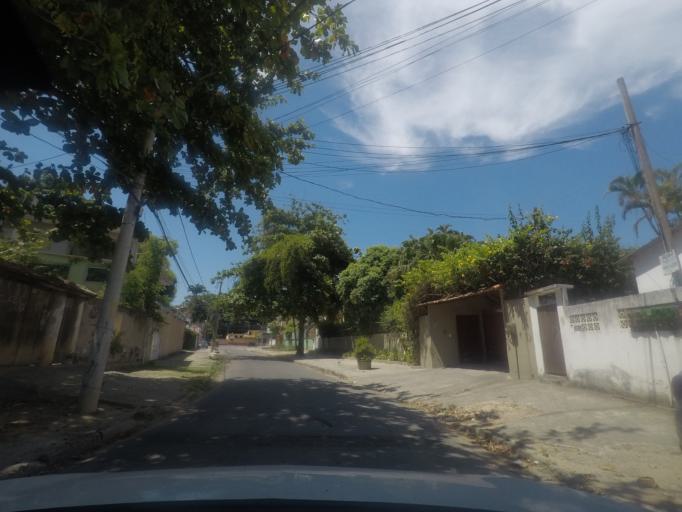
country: BR
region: Rio de Janeiro
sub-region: Itaguai
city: Itaguai
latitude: -23.0033
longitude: -43.6364
